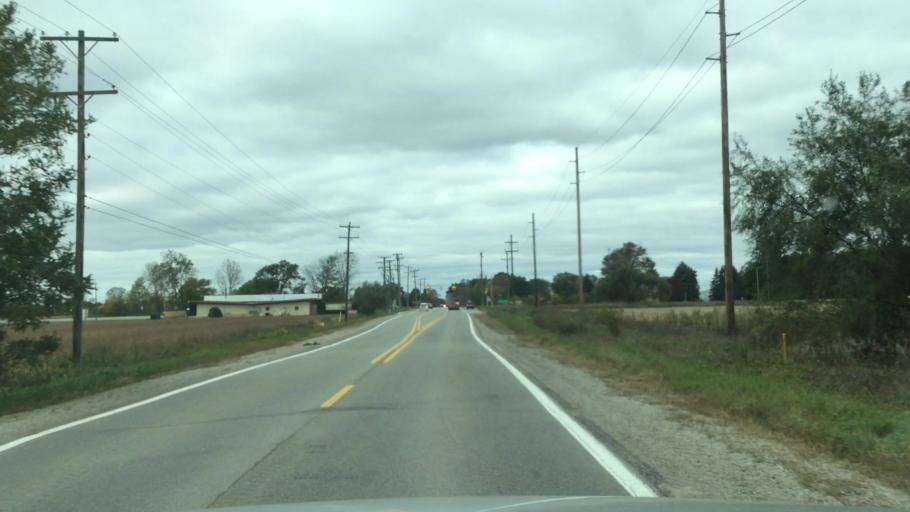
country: US
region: Michigan
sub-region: Macomb County
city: Armada
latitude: 42.8064
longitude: -82.8799
